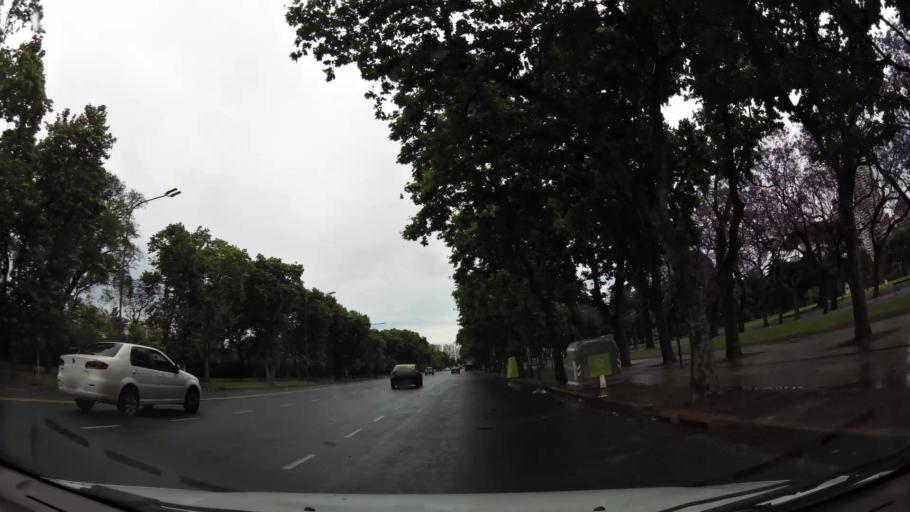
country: AR
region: Buenos Aires F.D.
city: Retiro
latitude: -34.5756
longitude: -58.4157
